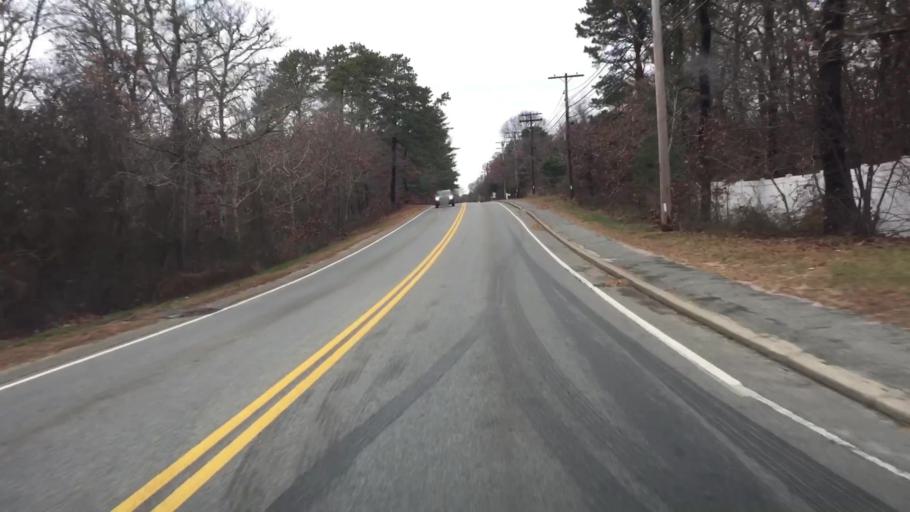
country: US
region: Massachusetts
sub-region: Barnstable County
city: Teaticket
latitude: 41.5744
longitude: -70.6052
